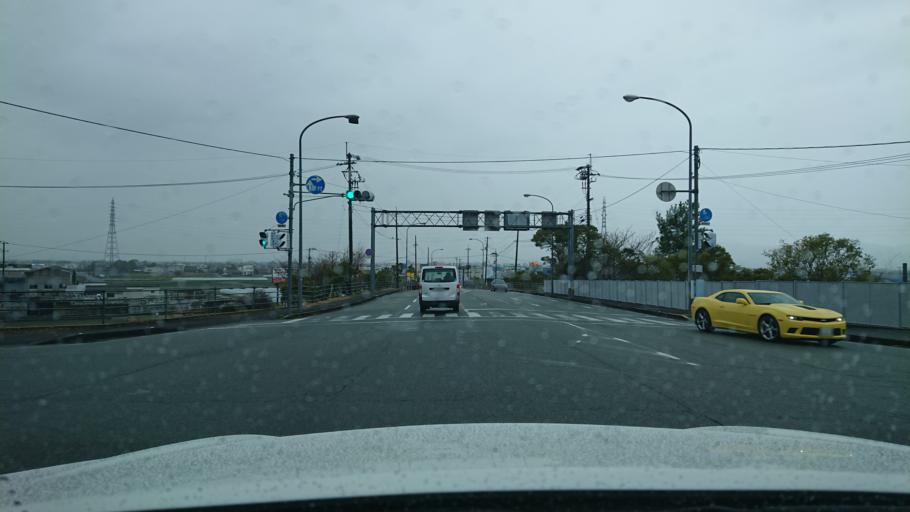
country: JP
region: Tokushima
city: Ishii
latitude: 34.0829
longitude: 134.5009
